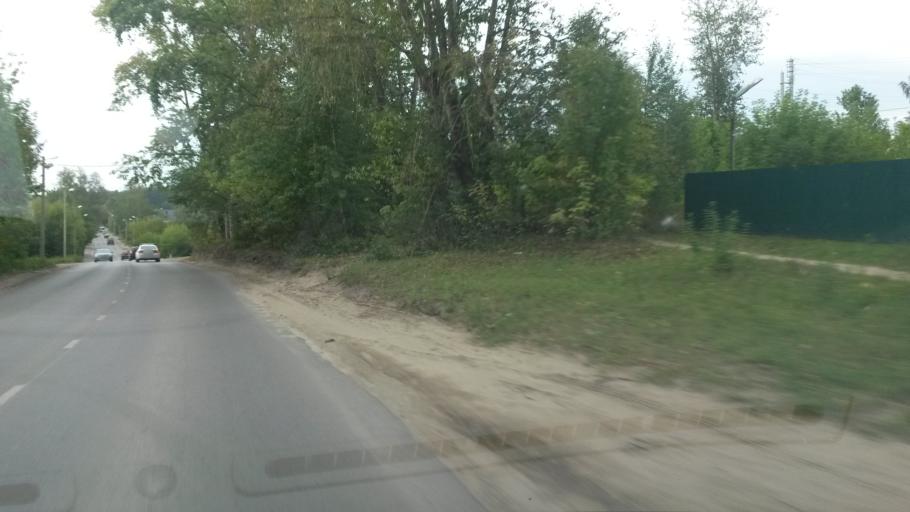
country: RU
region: Ivanovo
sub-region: Gorod Ivanovo
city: Ivanovo
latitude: 57.0294
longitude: 40.9257
